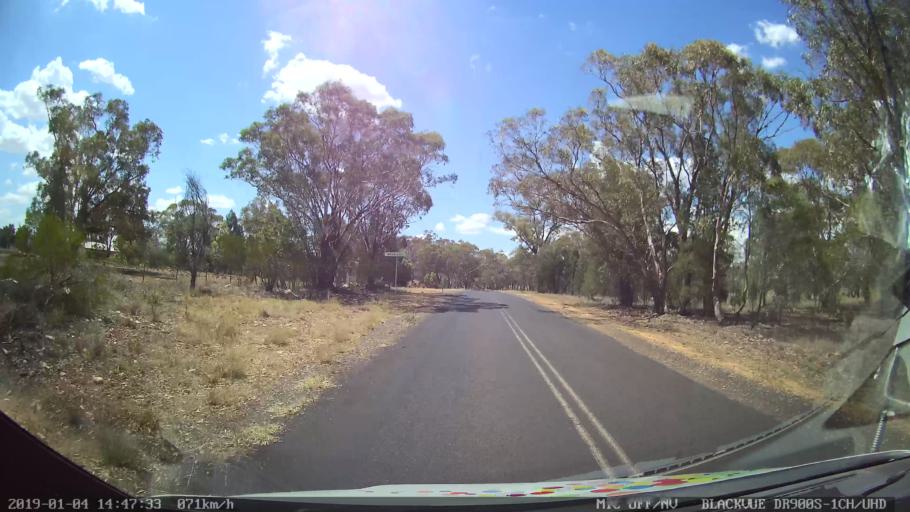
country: AU
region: New South Wales
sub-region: Dubbo Municipality
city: Dubbo
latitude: -32.0677
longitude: 148.6604
